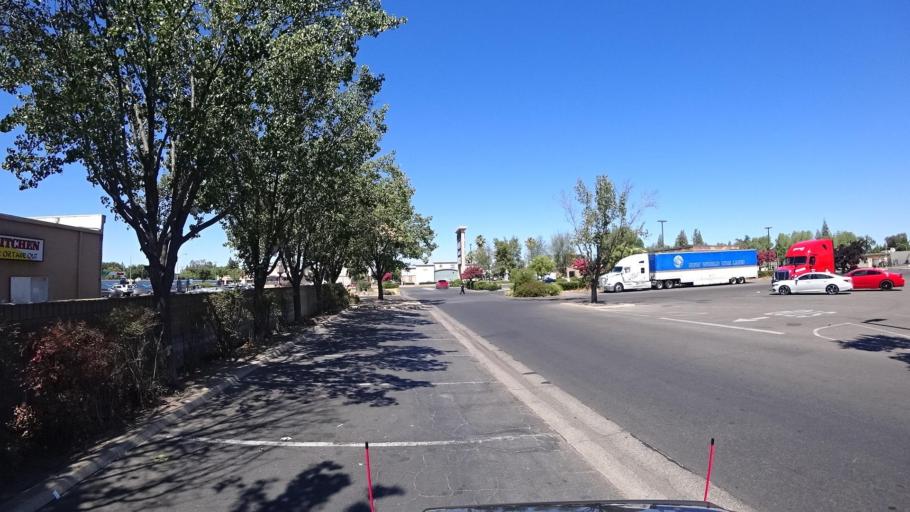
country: US
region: California
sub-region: Fresno County
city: Sunnyside
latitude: 36.7369
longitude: -119.6988
